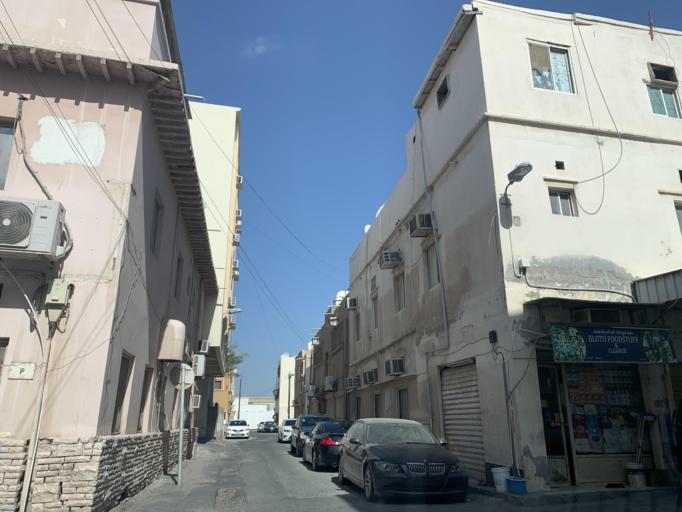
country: BH
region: Muharraq
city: Al Muharraq
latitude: 26.2585
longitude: 50.6172
